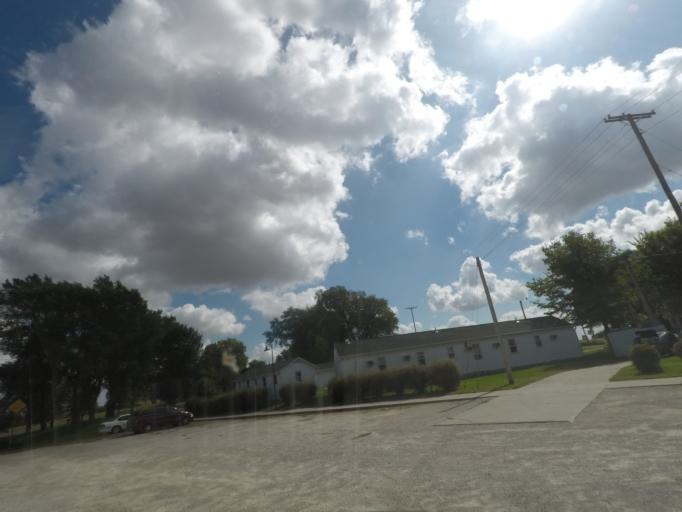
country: US
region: Iowa
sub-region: Story County
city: Nevada
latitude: 42.0230
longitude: -93.3108
